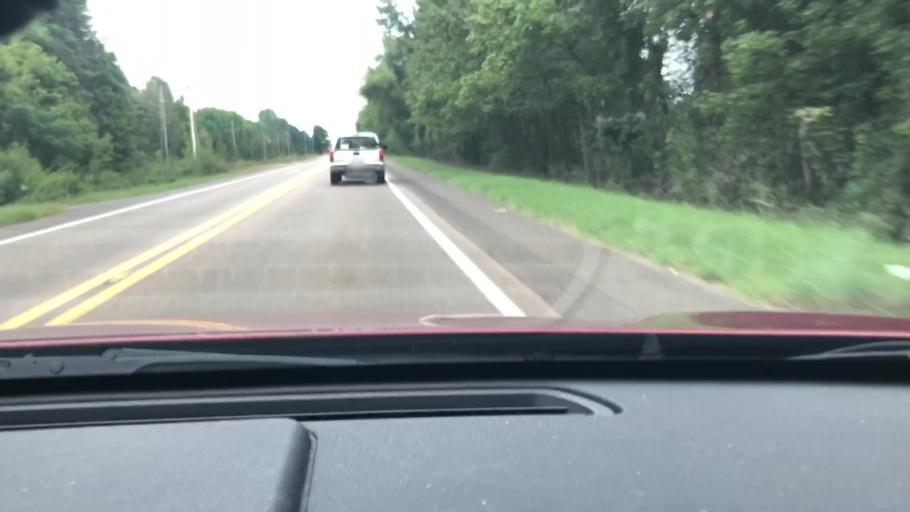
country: US
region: Arkansas
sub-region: Lafayette County
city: Lewisville
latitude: 33.3550
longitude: -93.6657
